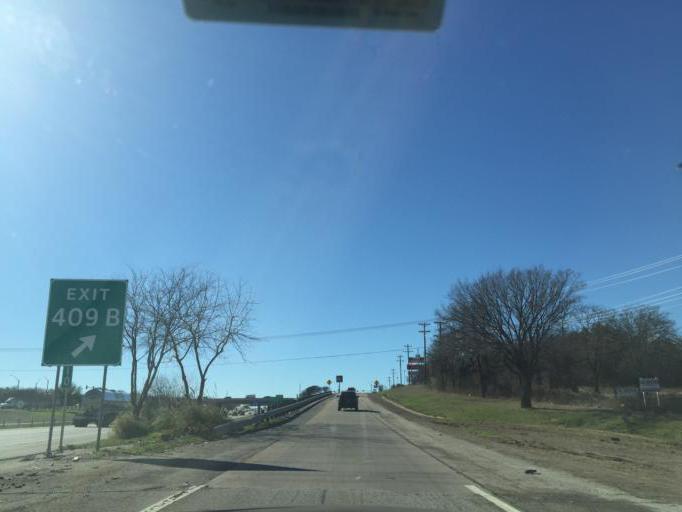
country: US
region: Texas
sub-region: Parker County
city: Weatherford
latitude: 32.7386
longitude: -97.7593
